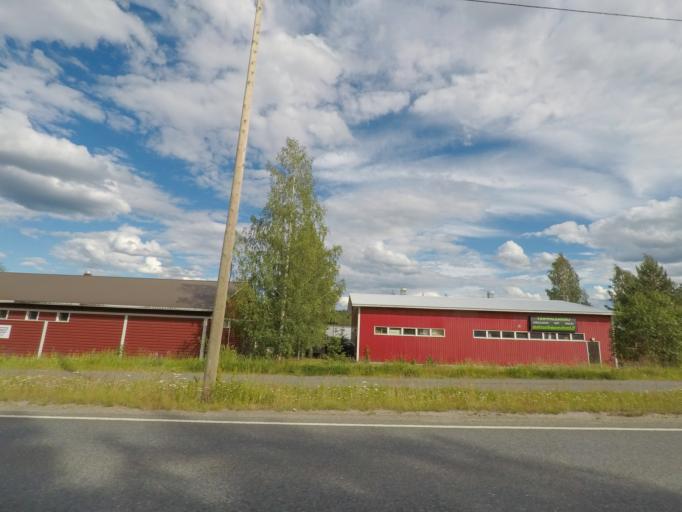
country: FI
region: Paijanne Tavastia
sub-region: Lahti
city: Lahti
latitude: 60.9534
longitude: 25.6150
